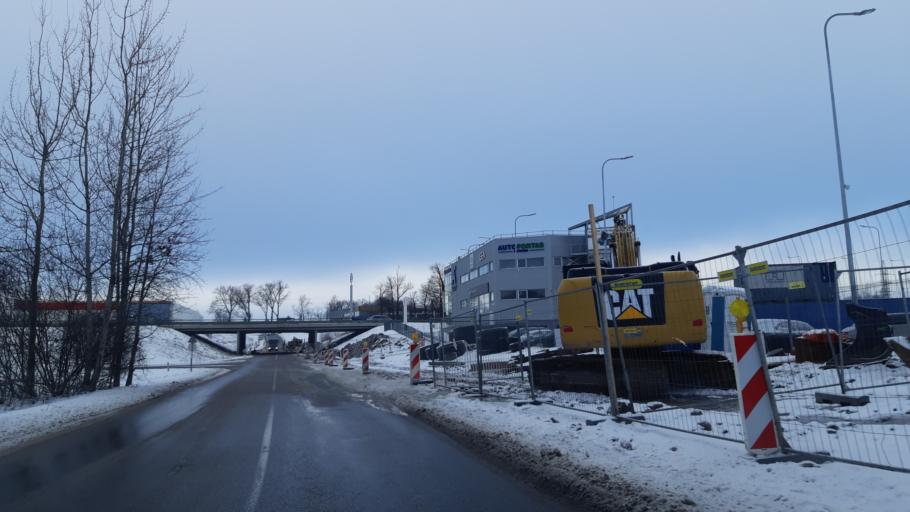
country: LT
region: Kauno apskritis
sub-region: Kaunas
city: Silainiai
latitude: 54.9354
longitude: 23.8749
